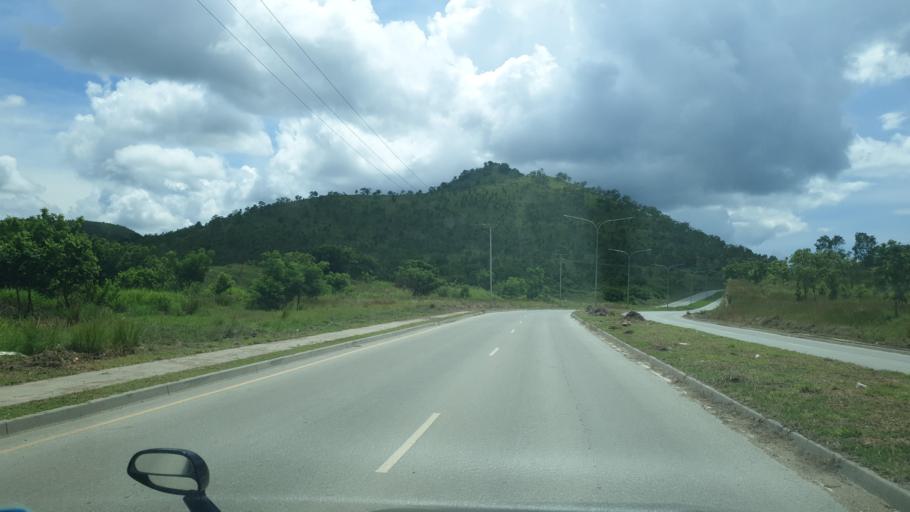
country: PG
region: National Capital
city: Port Moresby
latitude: -9.4202
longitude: 147.1365
